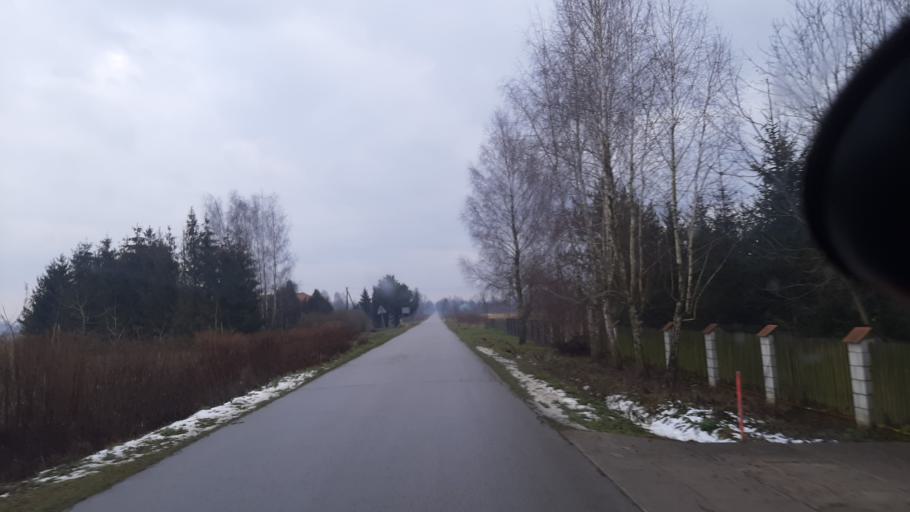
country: PL
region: Lublin Voivodeship
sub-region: Powiat lubelski
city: Lublin
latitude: 51.3395
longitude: 22.5387
